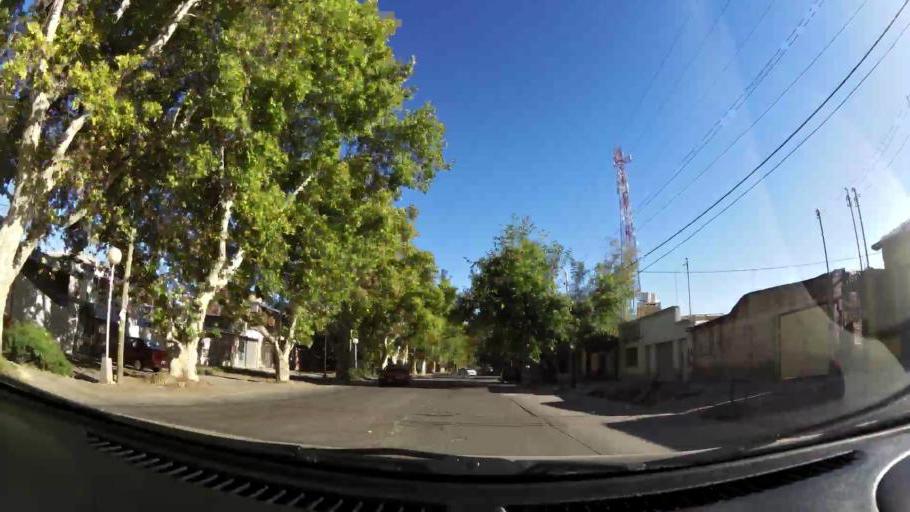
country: AR
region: Mendoza
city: Las Heras
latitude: -32.8535
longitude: -68.8269
